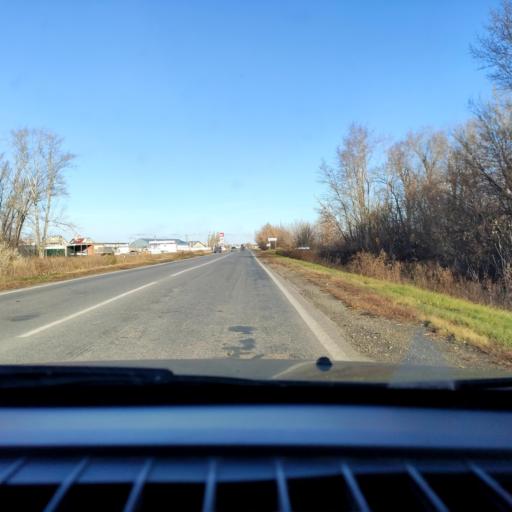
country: RU
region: Samara
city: Tol'yatti
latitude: 53.6310
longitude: 49.3028
